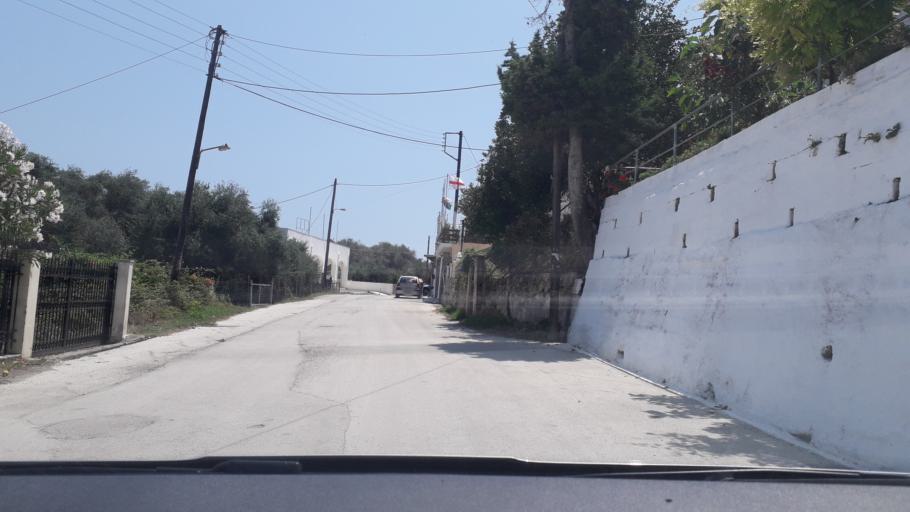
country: GR
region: Ionian Islands
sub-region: Nomos Kerkyras
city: Lefkimmi
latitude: 39.3817
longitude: 20.1140
